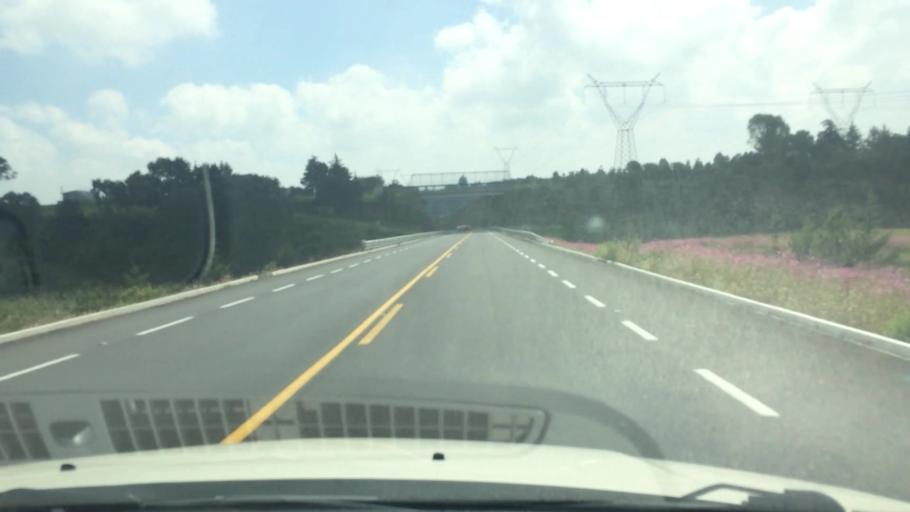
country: MX
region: Mexico
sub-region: Almoloya de Juarez
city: San Pedro de la Hortaliza (Ejido Almoloyan)
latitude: 19.3766
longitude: -99.8746
